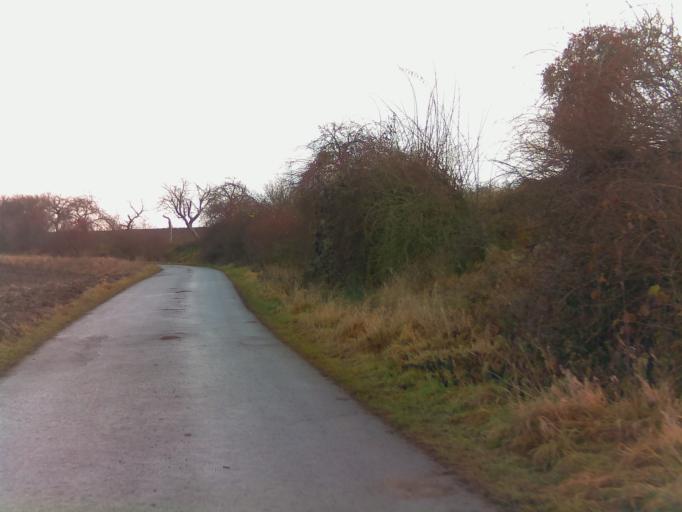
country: DE
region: Thuringia
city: Gumperda
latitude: 50.8054
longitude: 11.5092
